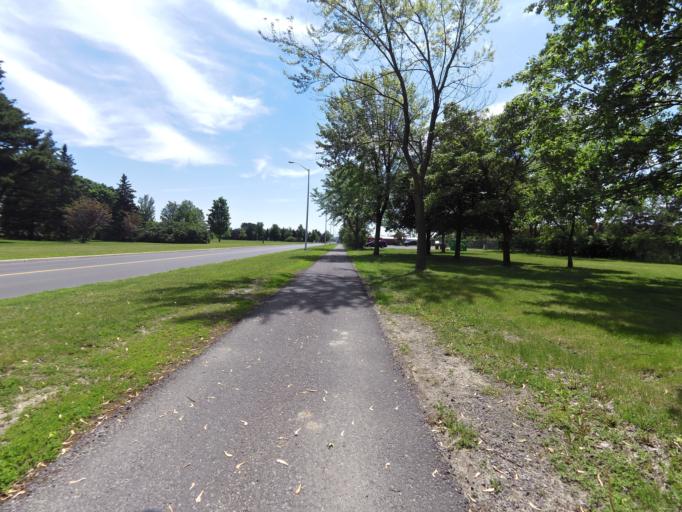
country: CA
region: Ontario
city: Ottawa
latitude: 45.3300
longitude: -75.6747
